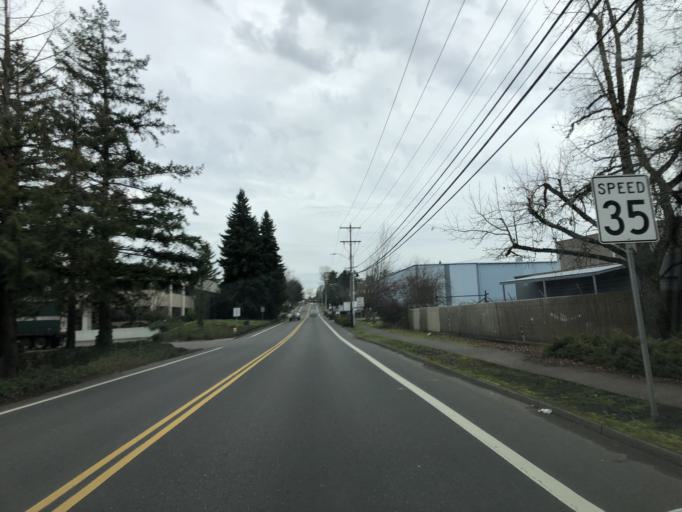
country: US
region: Oregon
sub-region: Washington County
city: Tigard
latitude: 45.4280
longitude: -122.7591
